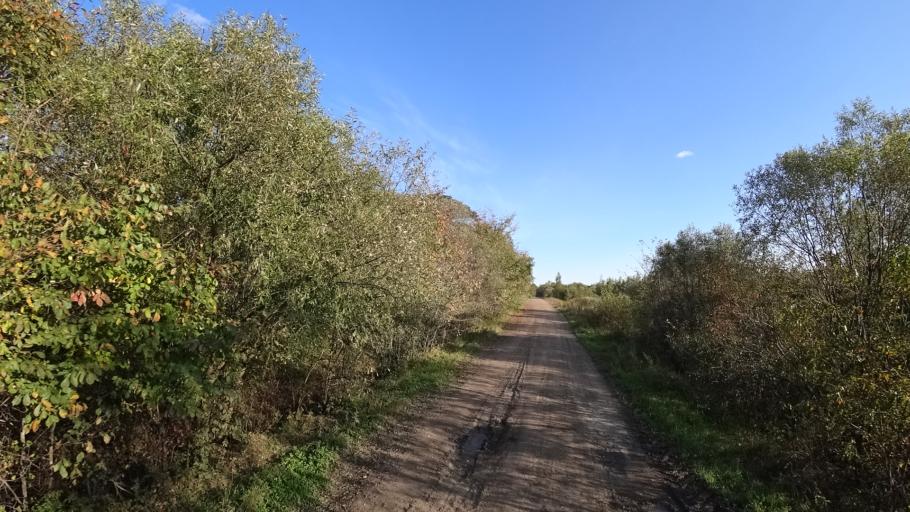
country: RU
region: Amur
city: Arkhara
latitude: 49.3497
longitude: 130.1151
